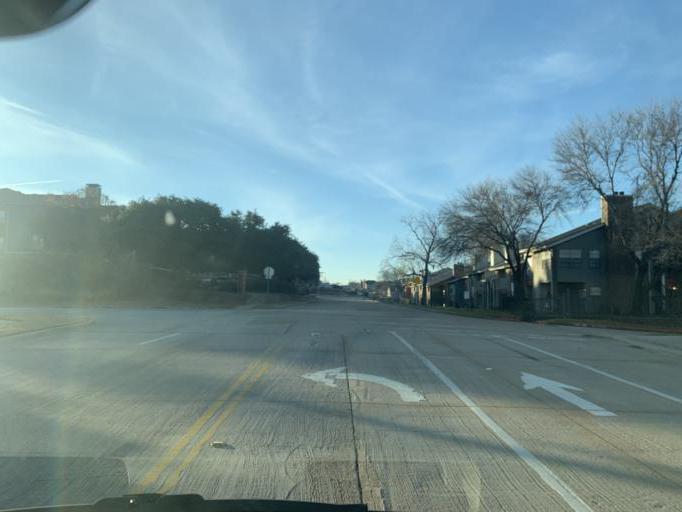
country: US
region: Texas
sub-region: Tarrant County
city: Euless
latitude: 32.7895
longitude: -97.0625
